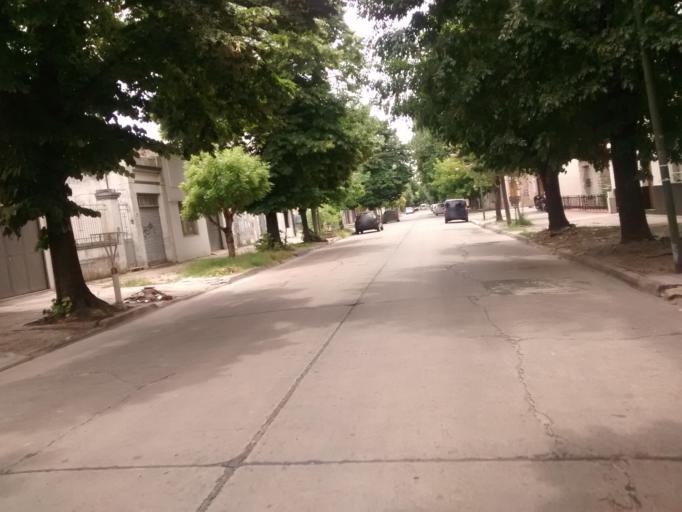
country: AR
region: Buenos Aires
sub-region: Partido de La Plata
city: La Plata
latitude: -34.9344
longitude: -57.9336
